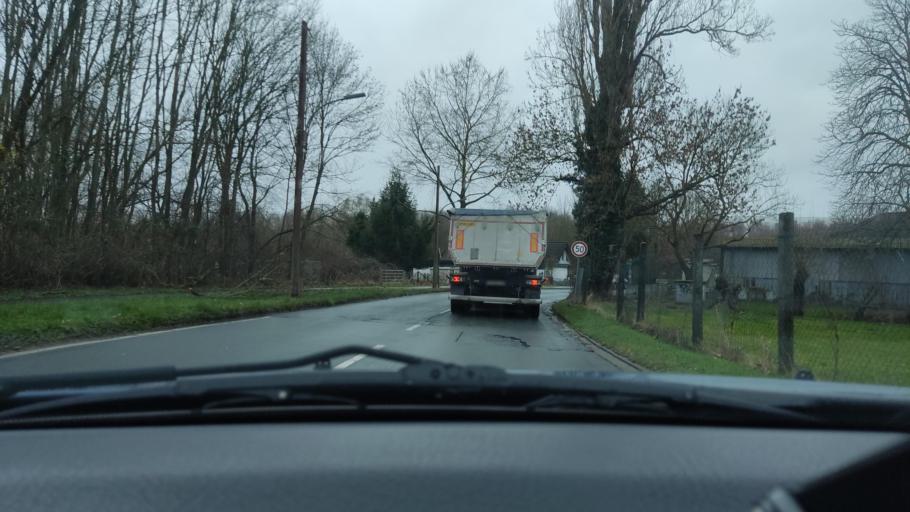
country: DE
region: North Rhine-Westphalia
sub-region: Regierungsbezirk Arnsberg
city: Dortmund
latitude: 51.5542
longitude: 7.4248
